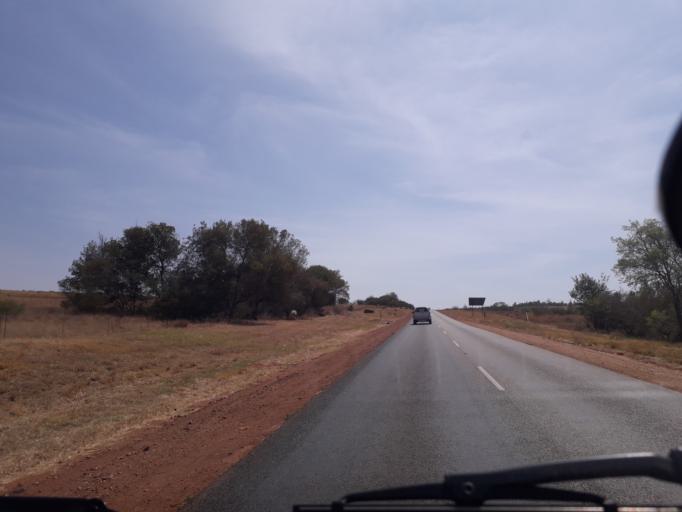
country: ZA
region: Gauteng
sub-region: West Rand District Municipality
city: Krugersdorp
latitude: -25.9961
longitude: 27.6998
